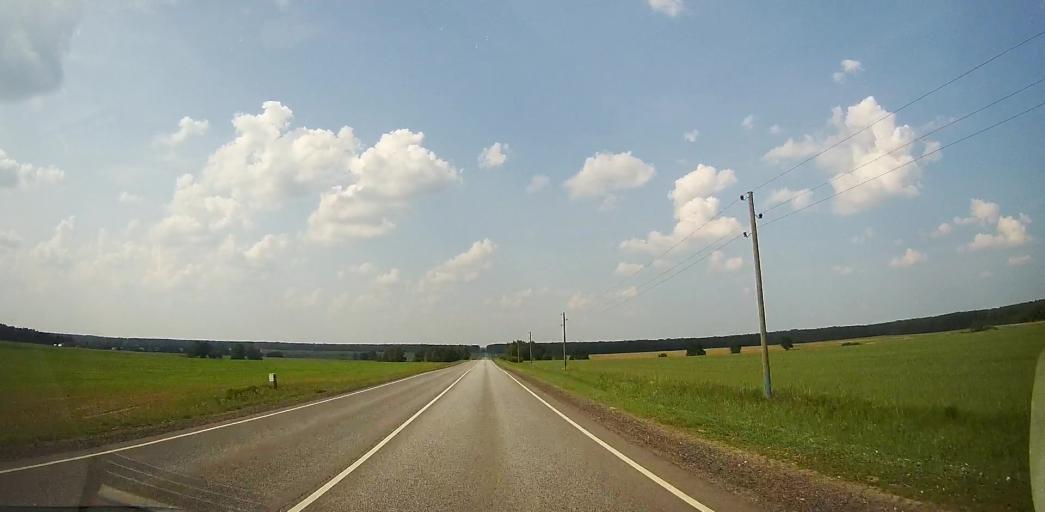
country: RU
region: Moskovskaya
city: Malino
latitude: 55.0373
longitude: 38.1555
